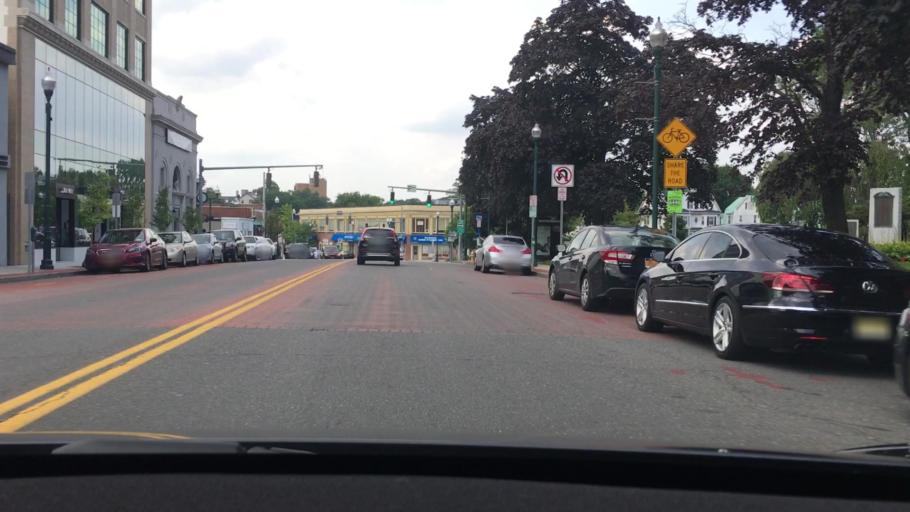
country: US
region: New York
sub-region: Westchester County
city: New Rochelle
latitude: 40.9198
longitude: -73.7868
